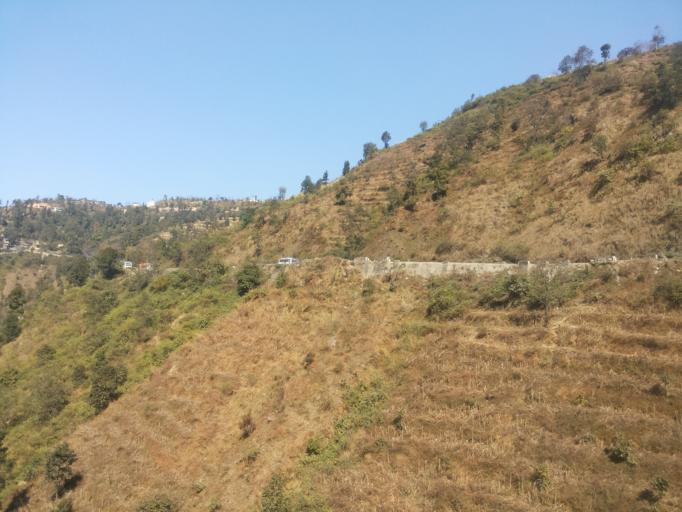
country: NP
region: Central Region
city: Kirtipur
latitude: 27.7074
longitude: 85.1999
